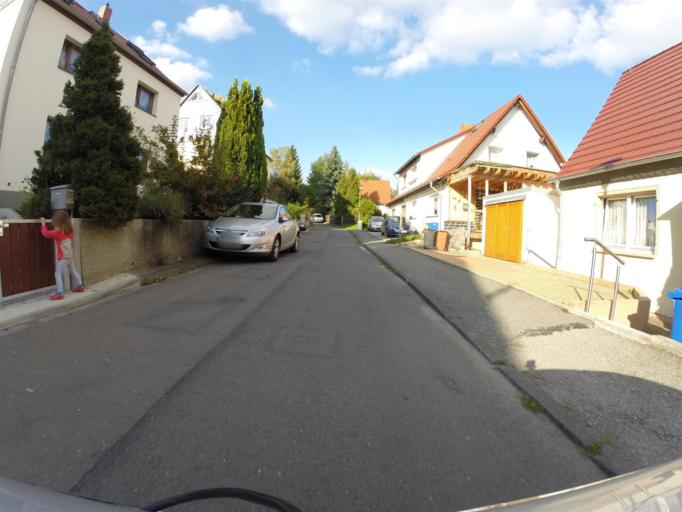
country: DE
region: Thuringia
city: Jena
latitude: 50.9480
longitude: 11.5987
